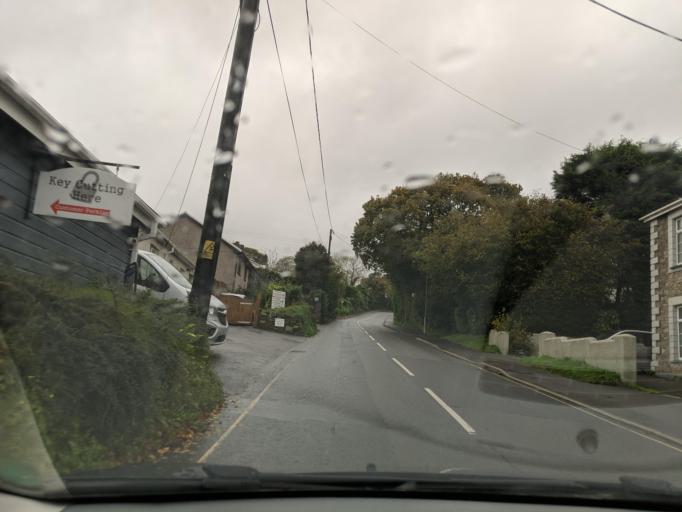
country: GB
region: England
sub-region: Cornwall
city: Bodmin
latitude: 50.4645
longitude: -4.7190
